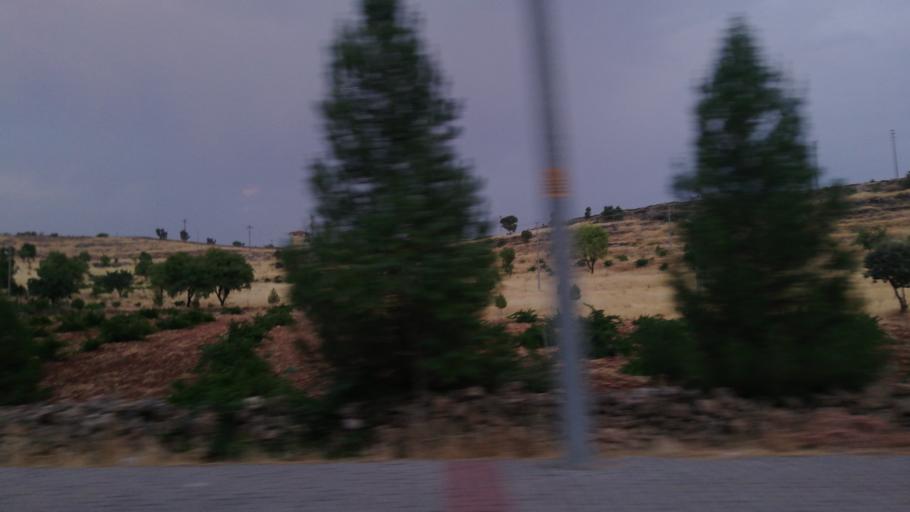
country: TR
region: Mardin
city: Kindirip
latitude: 37.4540
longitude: 41.2236
